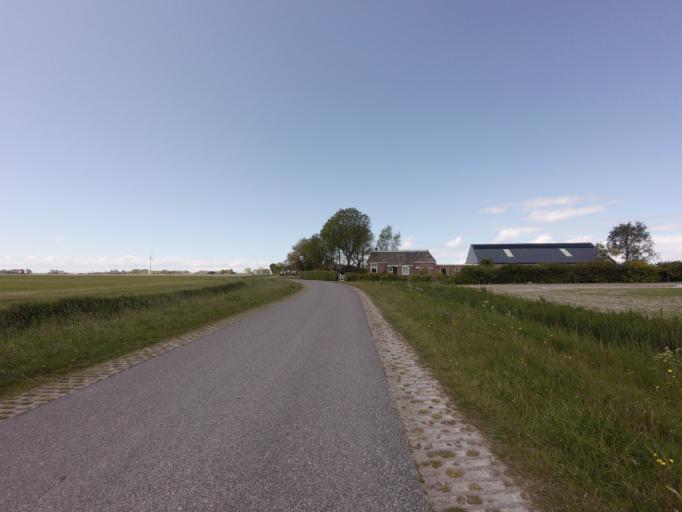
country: NL
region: Friesland
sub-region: Gemeente Harlingen
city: Harlingen
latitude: 53.1196
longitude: 5.4321
